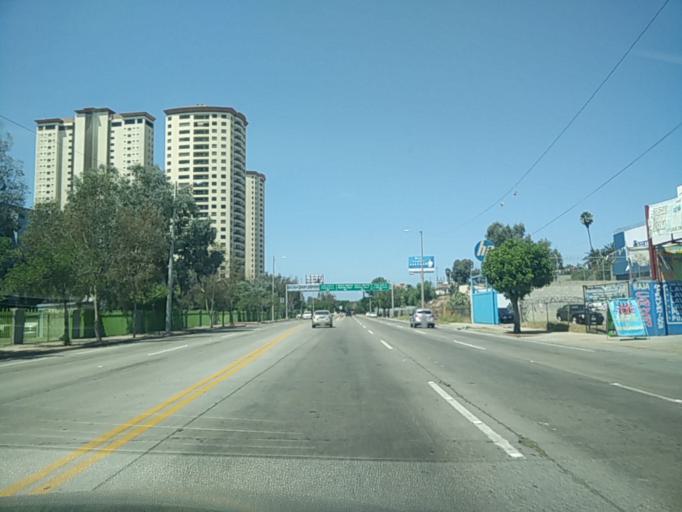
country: MX
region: Baja California
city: Tijuana
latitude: 32.5369
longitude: -117.0192
